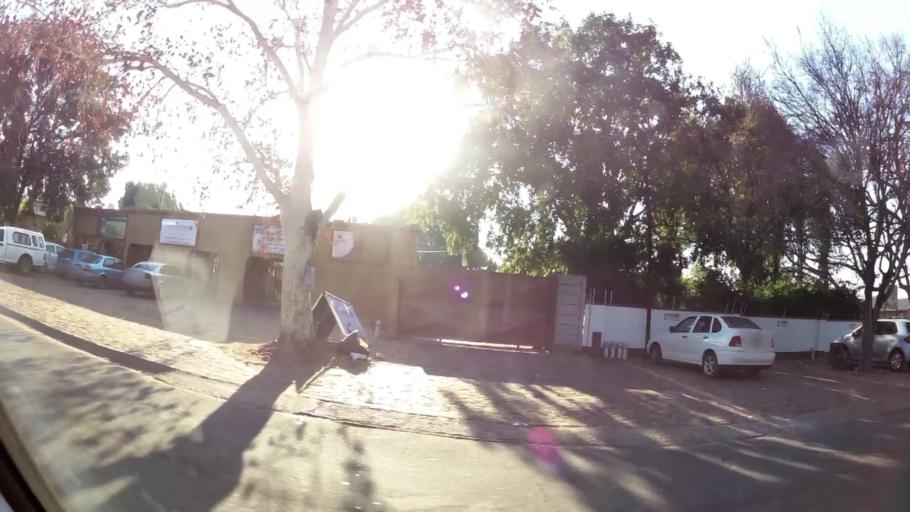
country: ZA
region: North-West
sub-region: Bojanala Platinum District Municipality
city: Rustenburg
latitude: -25.6755
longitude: 27.2368
